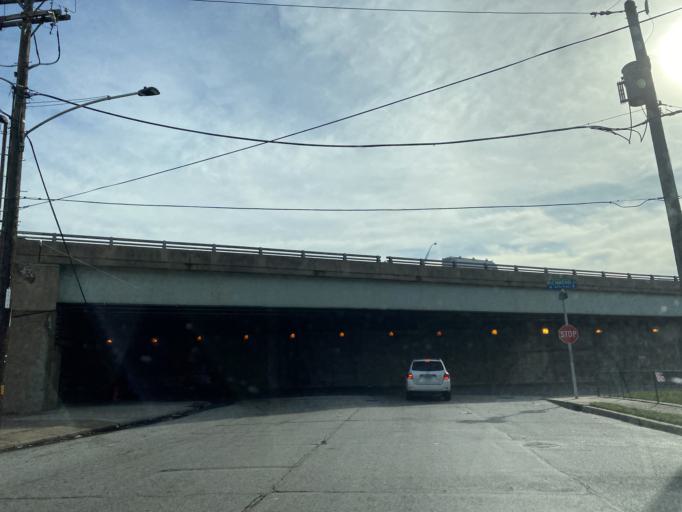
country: US
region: New Jersey
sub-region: Camden County
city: Pennsauken
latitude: 39.9906
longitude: -75.0874
